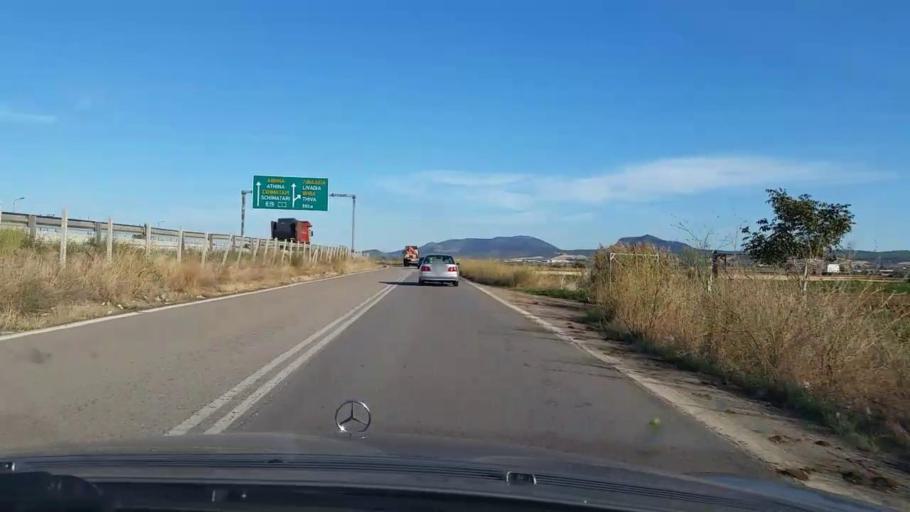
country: GR
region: Central Greece
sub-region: Nomos Voiotias
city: Thivai
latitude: 38.3648
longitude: 23.3120
